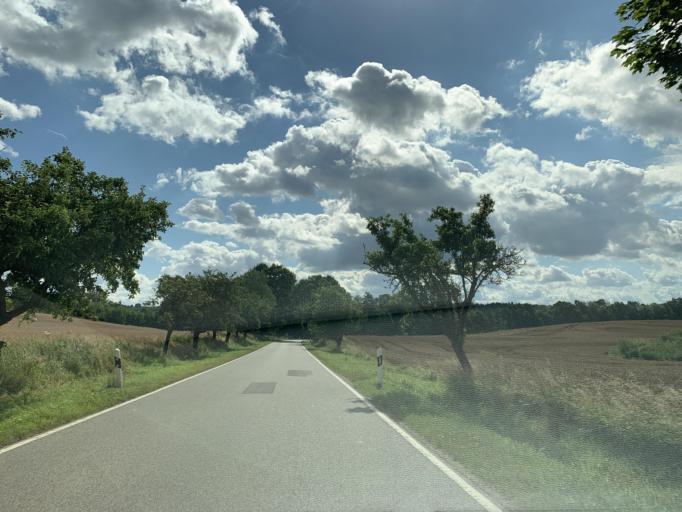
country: DE
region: Mecklenburg-Vorpommern
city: Neustrelitz
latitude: 53.4044
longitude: 13.1206
